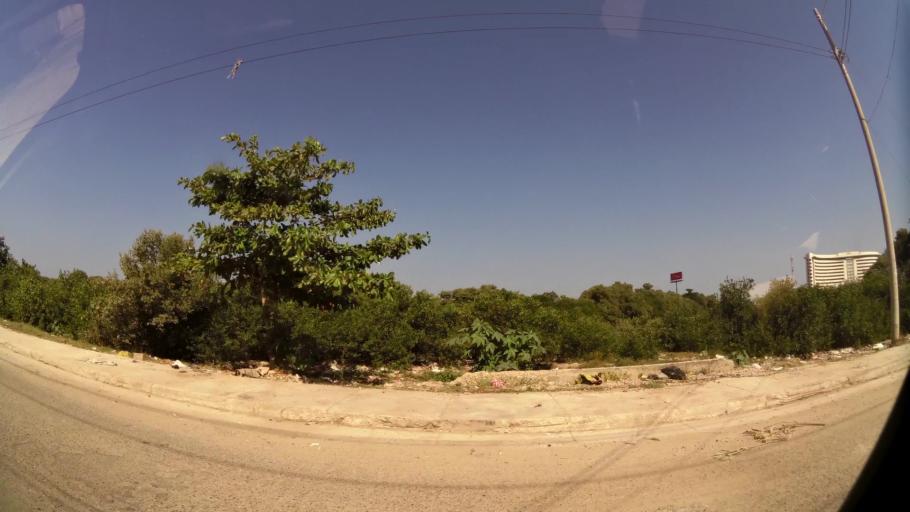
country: CO
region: Bolivar
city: Cartagena
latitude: 10.4391
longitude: -75.5268
